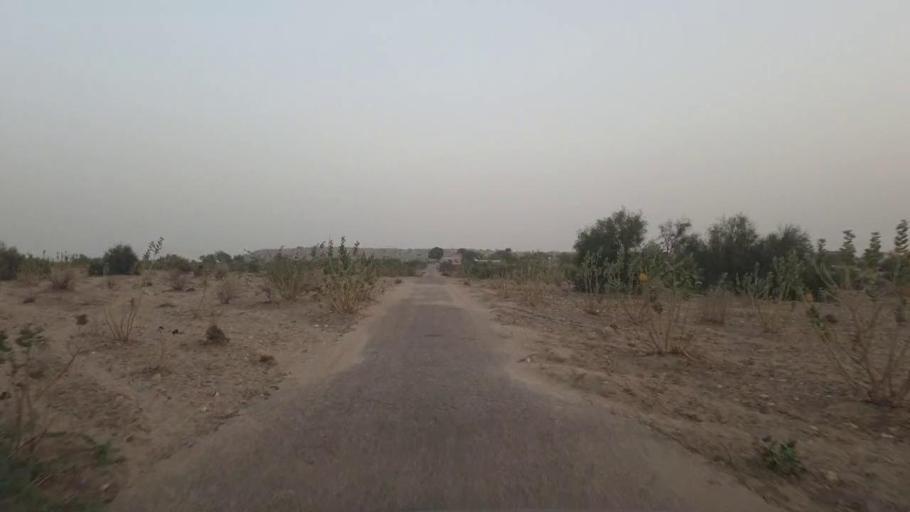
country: PK
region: Sindh
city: Chor
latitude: 25.5023
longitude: 69.8215
